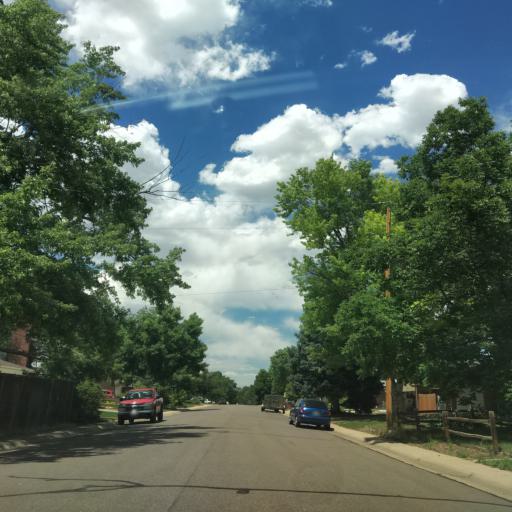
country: US
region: Colorado
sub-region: Jefferson County
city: Lakewood
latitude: 39.6859
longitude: -105.0956
